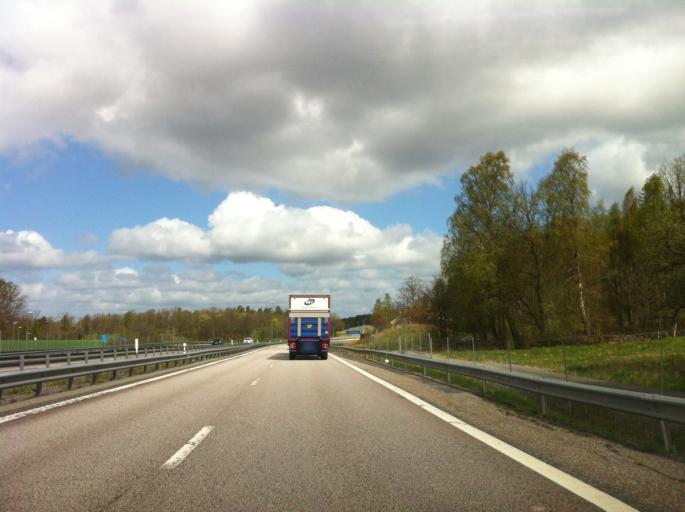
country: SE
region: Vaestra Goetaland
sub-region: Alingsas Kommun
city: Ingared
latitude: 57.8935
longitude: 12.4887
